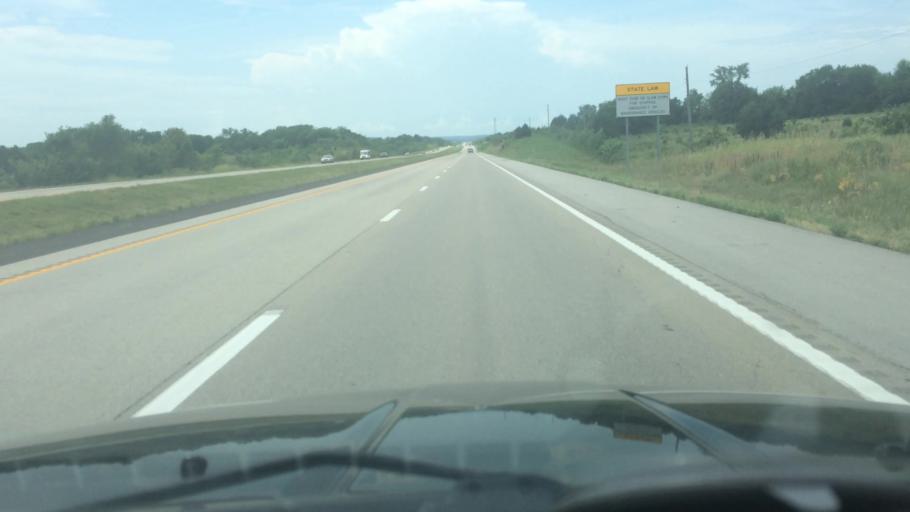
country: US
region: Missouri
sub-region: Polk County
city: Humansville
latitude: 37.7671
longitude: -93.5620
